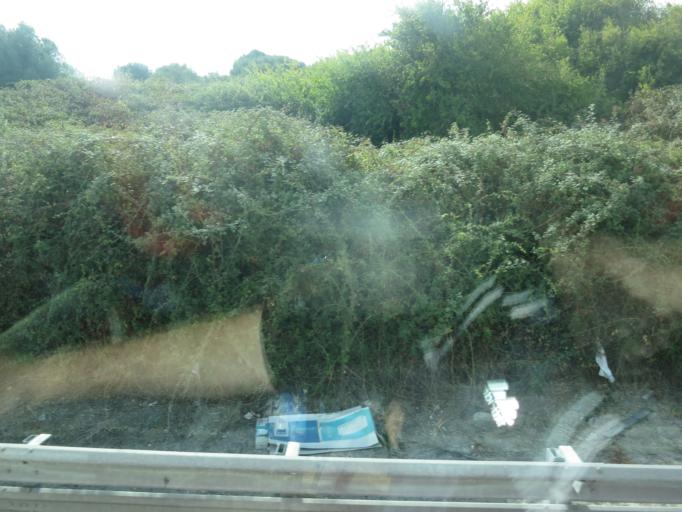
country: ES
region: Andalusia
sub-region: Provincia de Cadiz
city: Algeciras
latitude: 36.0985
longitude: -5.4676
